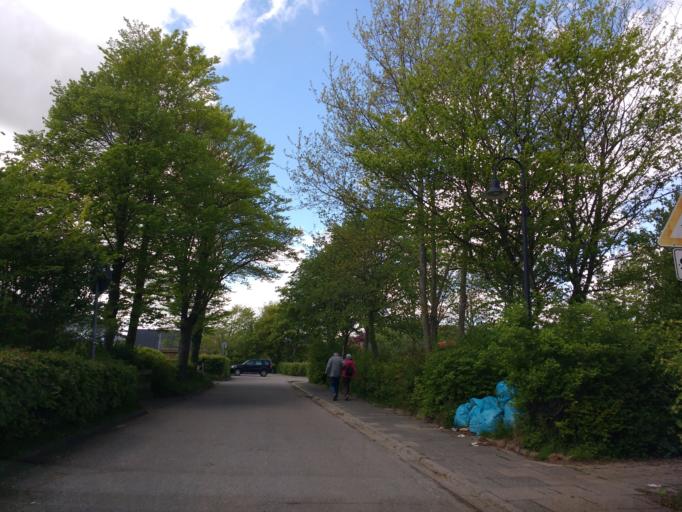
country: DE
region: Schleswig-Holstein
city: Damp
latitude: 54.5802
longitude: 10.0201
